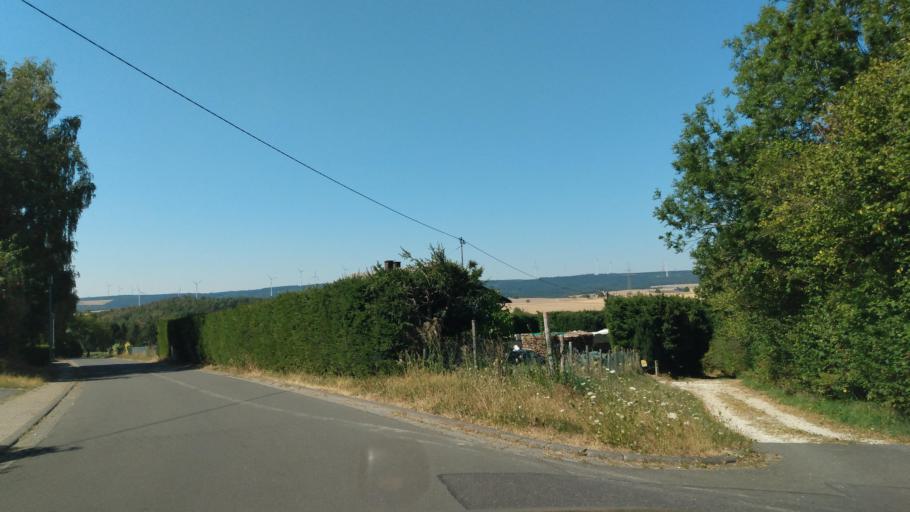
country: DE
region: Rheinland-Pfalz
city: Rorodt
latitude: 49.7867
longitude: 7.0727
